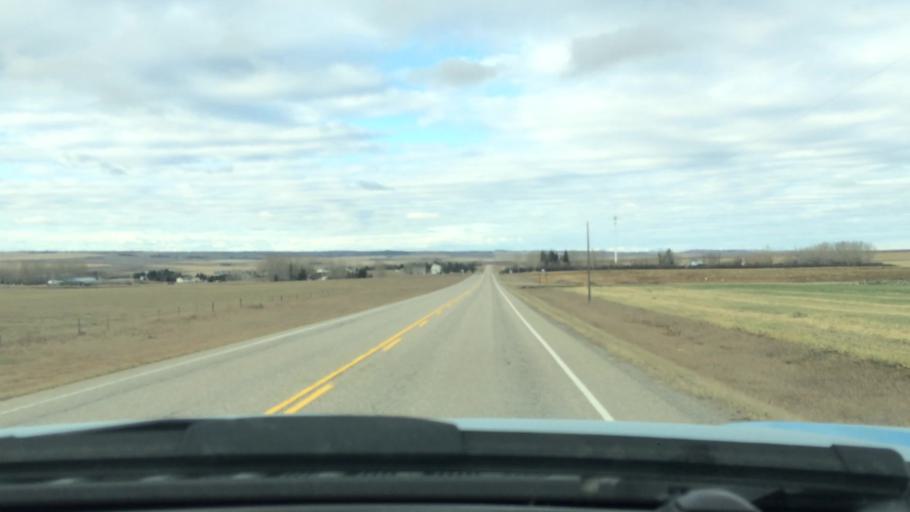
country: CA
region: Alberta
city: Airdrie
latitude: 51.2116
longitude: -114.1357
